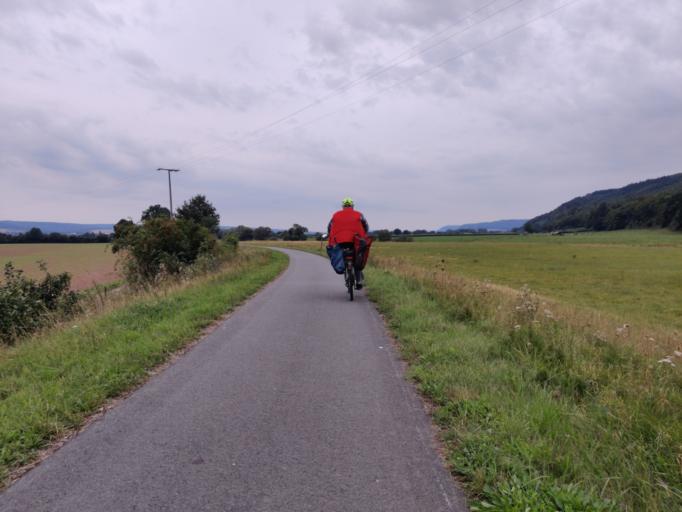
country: DE
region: Lower Saxony
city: Bevern
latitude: 51.8639
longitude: 9.4620
